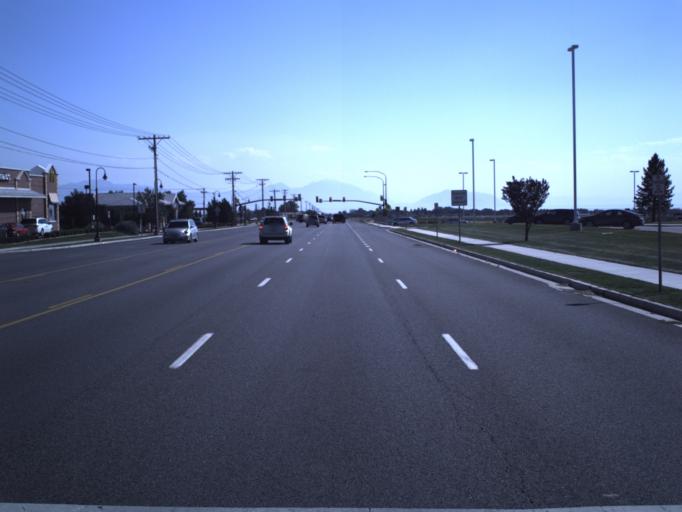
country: US
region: Utah
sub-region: Utah County
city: Cedar Hills
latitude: 40.4176
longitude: -111.7736
